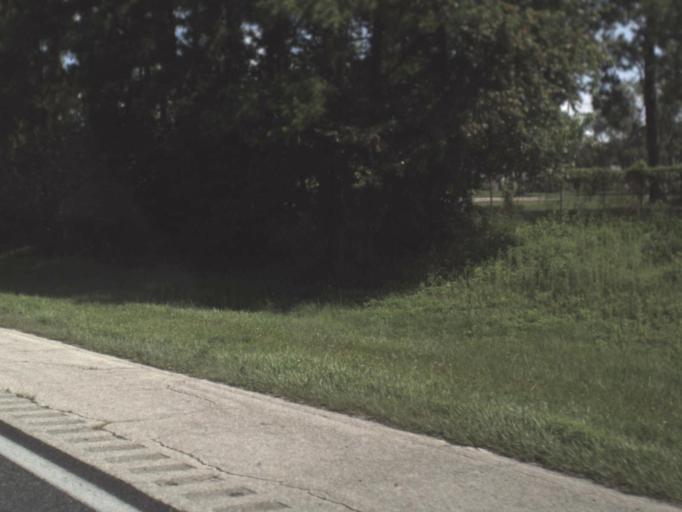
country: US
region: Florida
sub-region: Alachua County
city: Alachua
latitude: 29.6773
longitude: -82.4350
